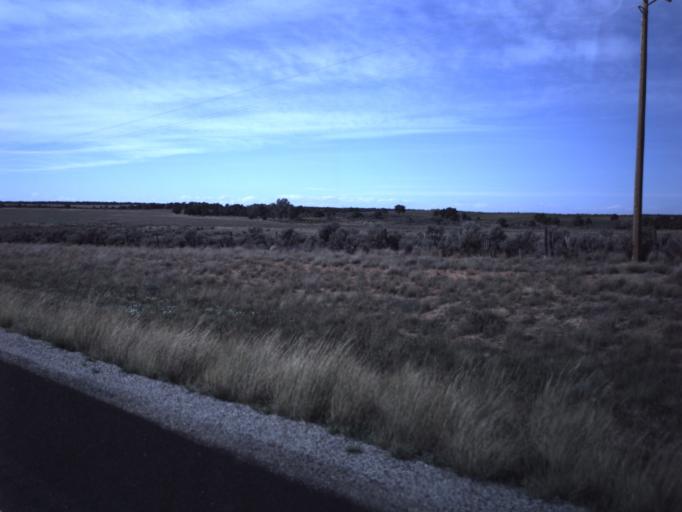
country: US
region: Utah
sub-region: San Juan County
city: Monticello
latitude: 37.8524
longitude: -109.1746
